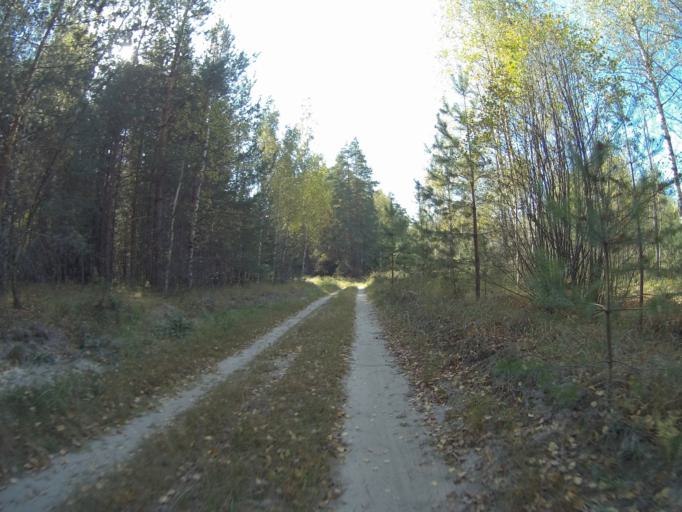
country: RU
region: Vladimir
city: Vorsha
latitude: 55.9716
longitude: 40.1345
